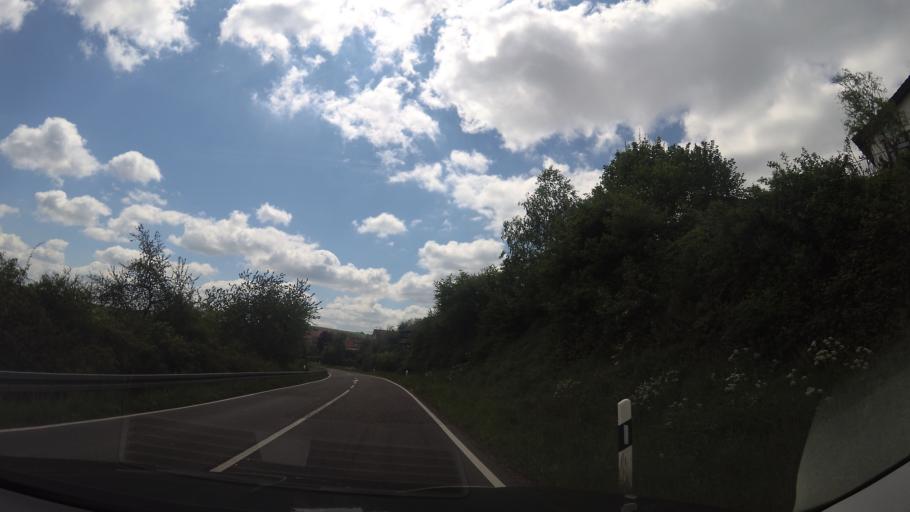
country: DE
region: Saarland
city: Lebach
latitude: 49.4182
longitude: 6.9216
